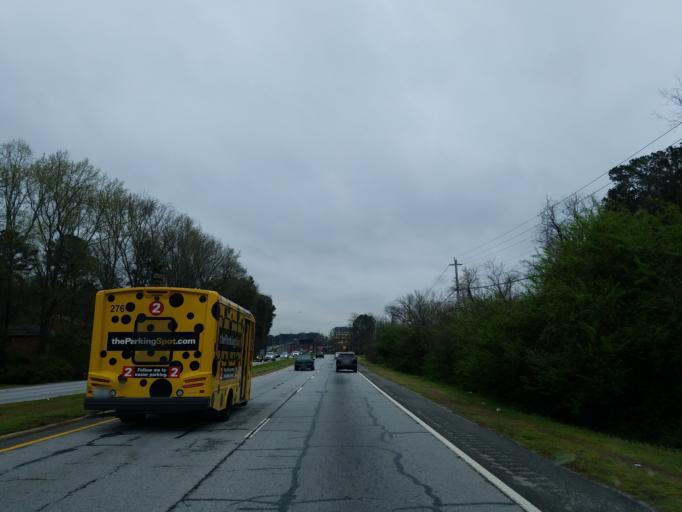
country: US
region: Georgia
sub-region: Fulton County
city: College Park
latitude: 33.6522
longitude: -84.4860
